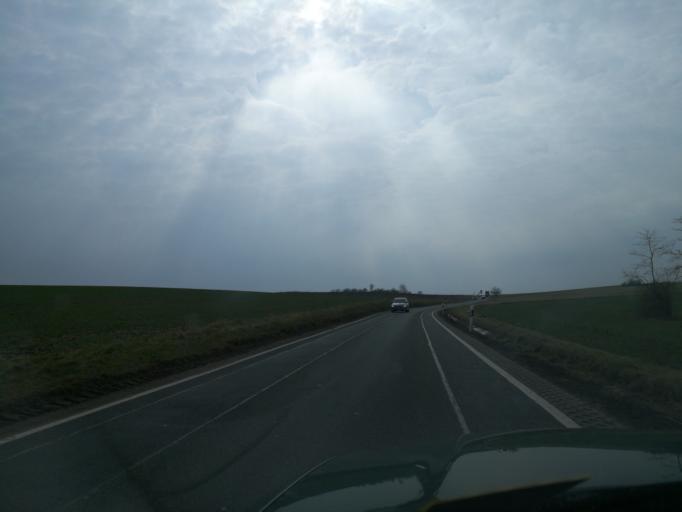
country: DE
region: Bavaria
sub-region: Regierungsbezirk Mittelfranken
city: Obermichelbach
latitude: 49.5045
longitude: 10.9460
